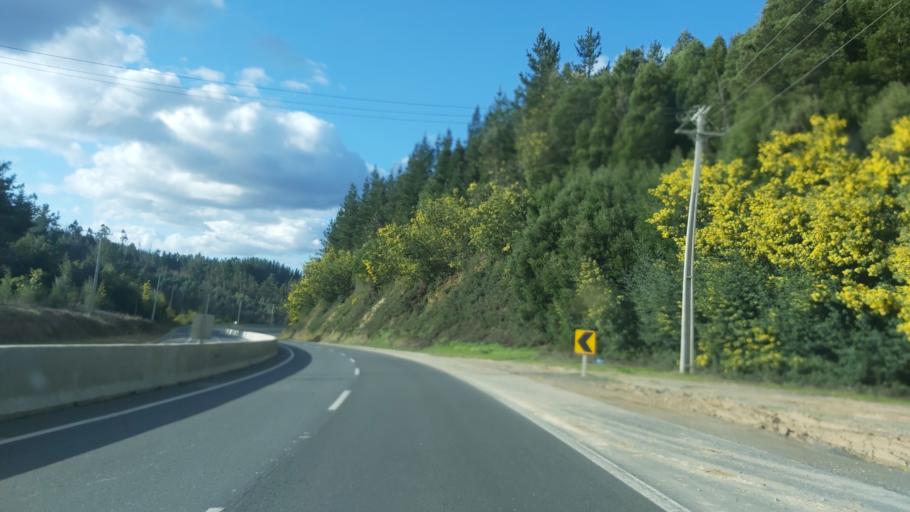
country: CL
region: Biobio
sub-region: Provincia de Concepcion
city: Chiguayante
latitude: -36.8522
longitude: -72.9080
